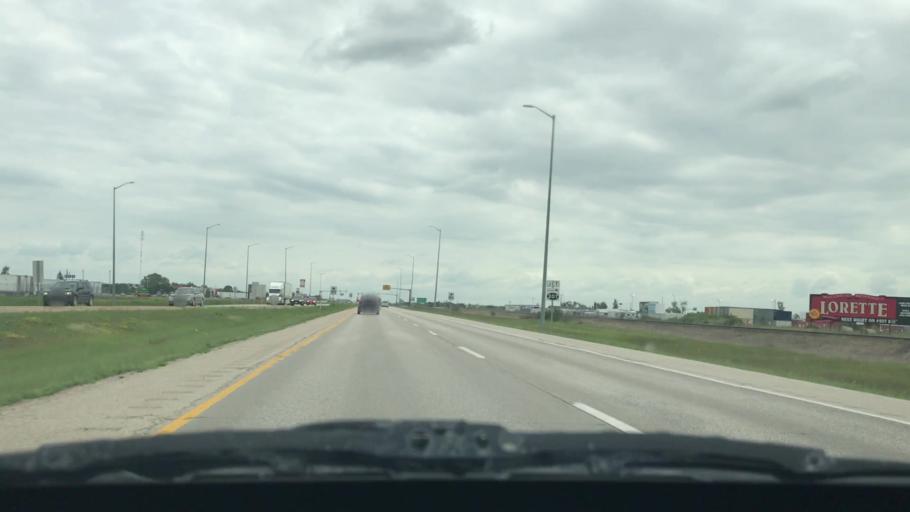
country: CA
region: Manitoba
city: Winnipeg
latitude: 49.8226
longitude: -96.9420
